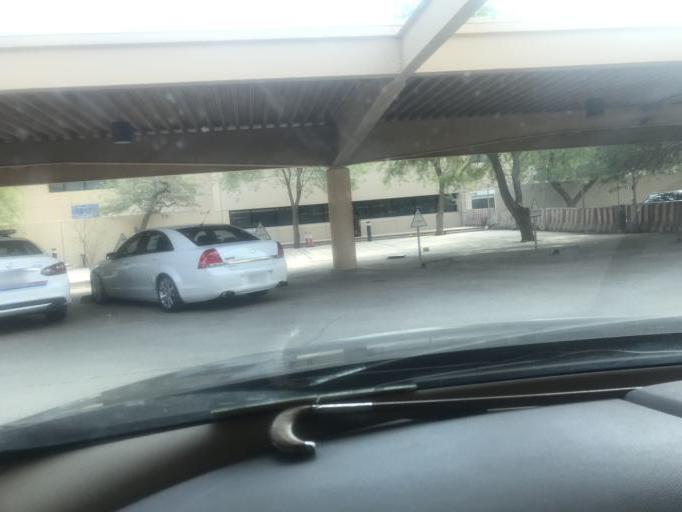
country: SA
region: Ar Riyad
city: Riyadh
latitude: 24.9697
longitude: 46.6960
